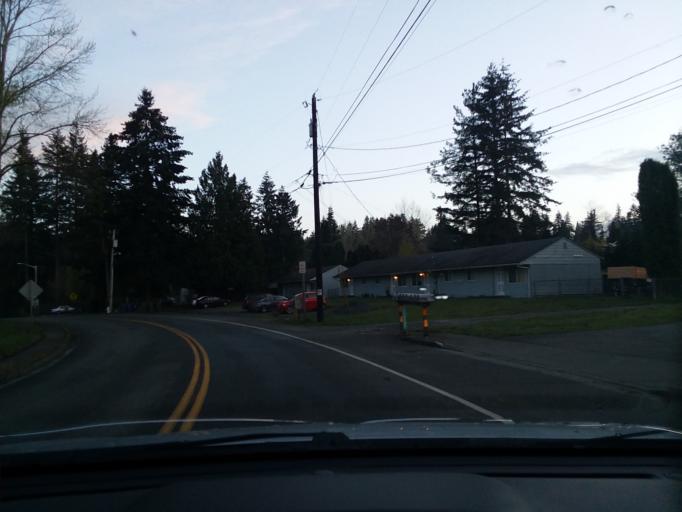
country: US
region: Washington
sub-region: Snohomish County
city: Brier
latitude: 47.7781
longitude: -122.2533
